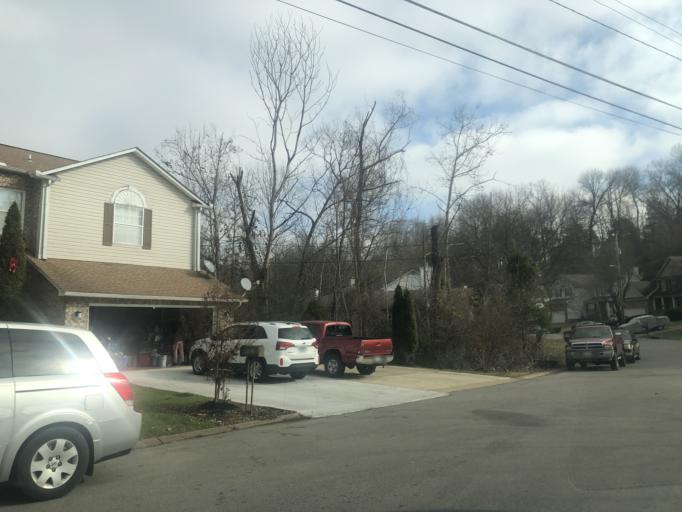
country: US
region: Tennessee
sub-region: Rutherford County
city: La Vergne
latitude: 36.0804
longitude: -86.6536
